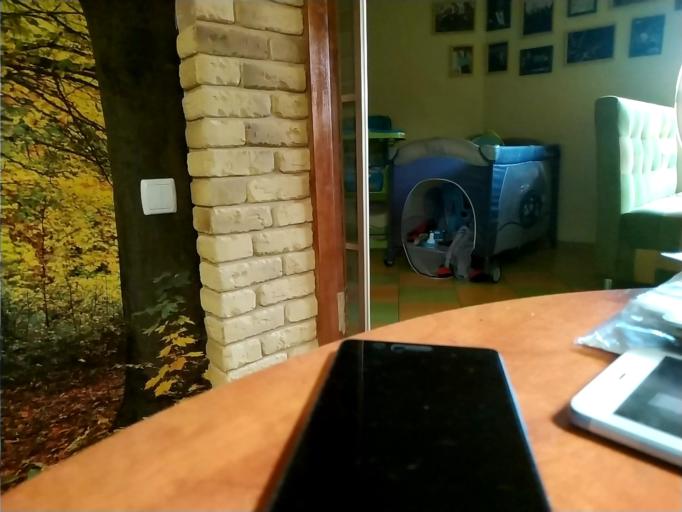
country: RU
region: Kaluga
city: Duminichi
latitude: 53.7146
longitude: 35.4258
